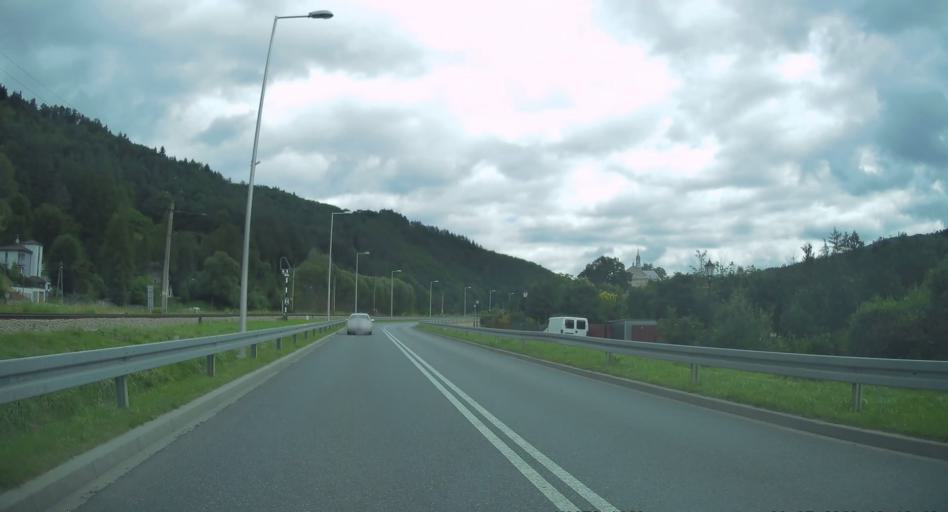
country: PL
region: Lesser Poland Voivodeship
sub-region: Powiat nowosadecki
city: Muszyna
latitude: 49.3587
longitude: 20.8984
